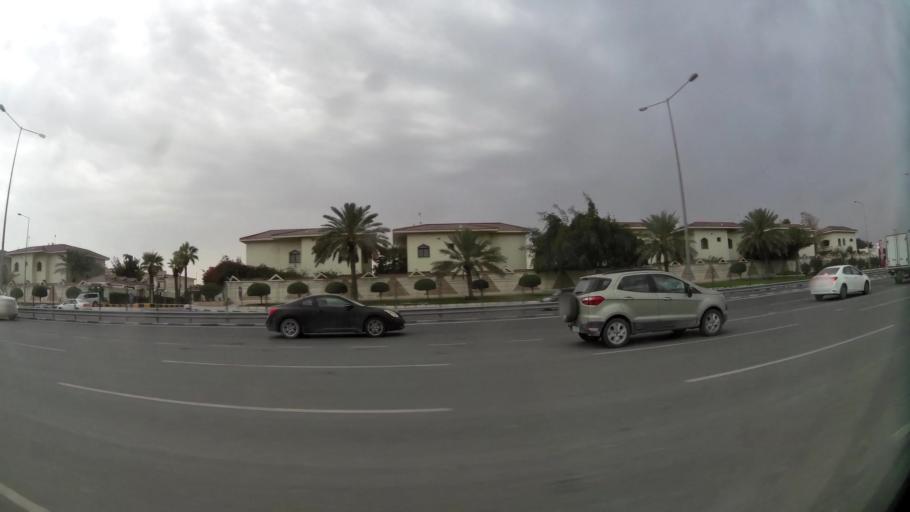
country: QA
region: Baladiyat ad Dawhah
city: Doha
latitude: 25.2706
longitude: 51.5124
